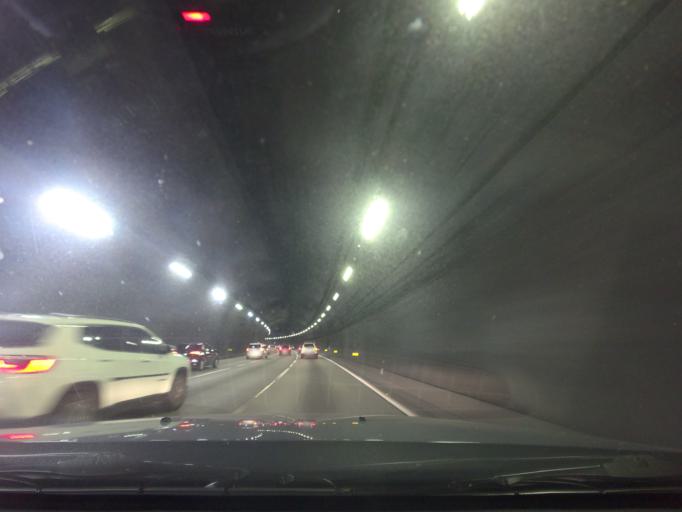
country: BR
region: Sao Paulo
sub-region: Cubatao
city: Cubatao
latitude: -23.8879
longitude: -46.5045
